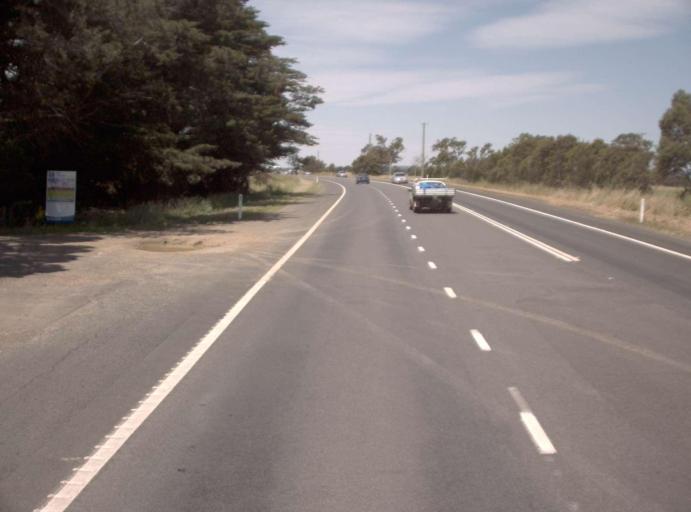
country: AU
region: Victoria
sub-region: Latrobe
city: Traralgon
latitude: -38.1589
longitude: 146.7232
